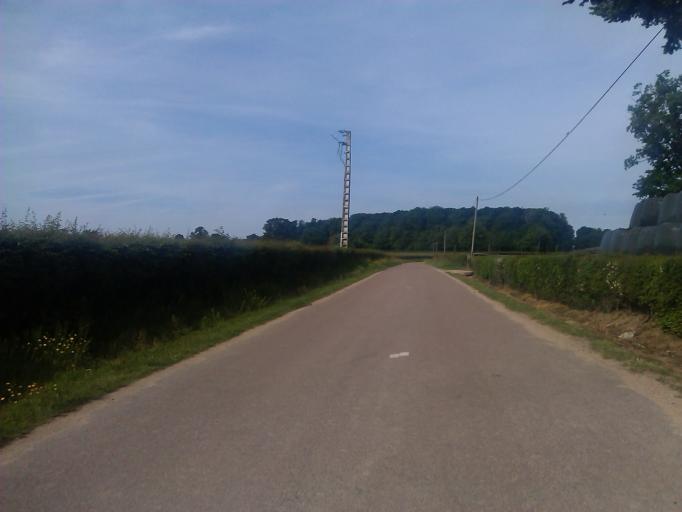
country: FR
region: Auvergne
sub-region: Departement de l'Allier
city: Cerilly
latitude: 46.6165
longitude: 2.7452
